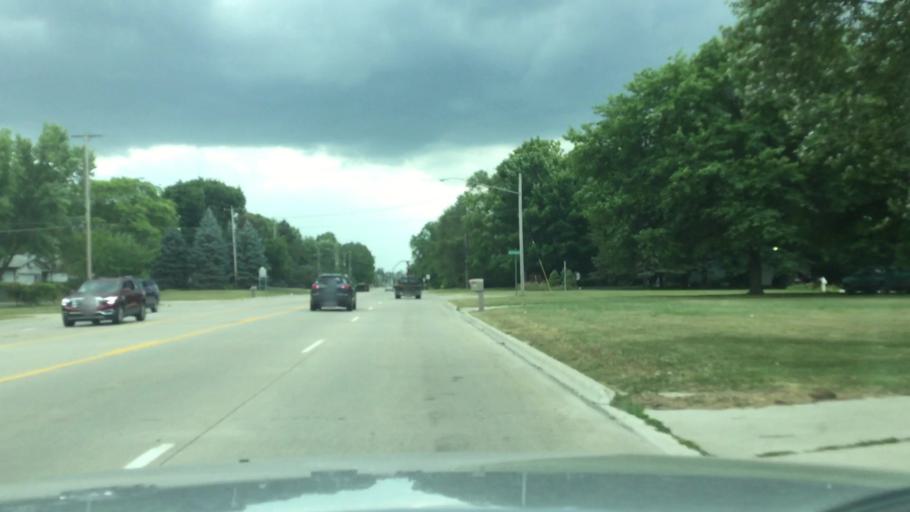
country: US
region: Michigan
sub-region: Genesee County
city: Flint
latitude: 43.0237
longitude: -83.7734
